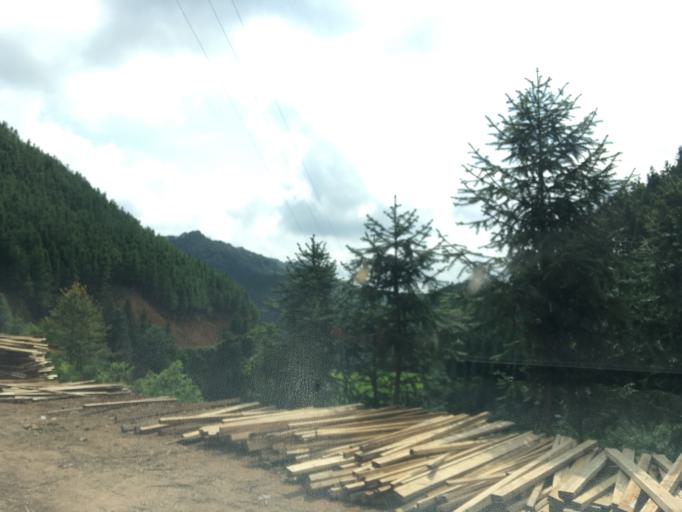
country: CN
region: Guangxi Zhuangzu Zizhiqu
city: Xinzhou
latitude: 24.8681
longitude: 105.8617
